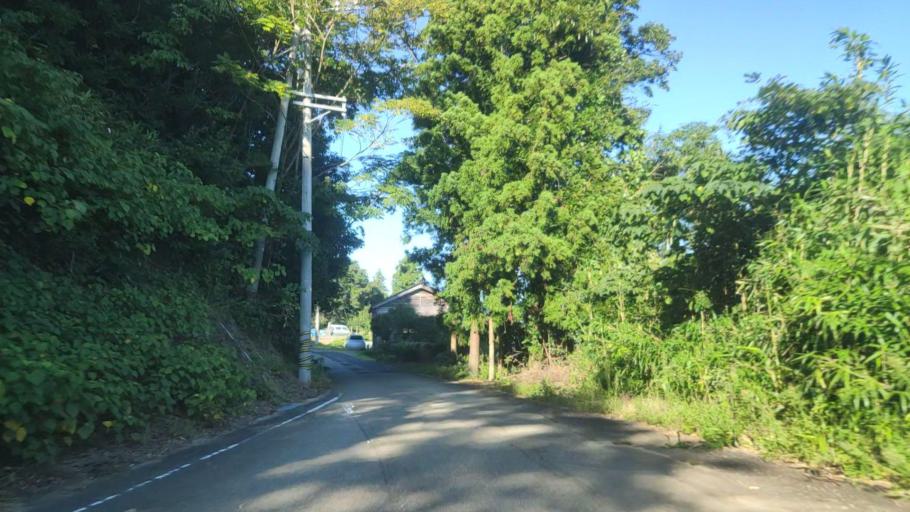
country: JP
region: Ishikawa
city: Nanao
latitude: 37.1189
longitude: 136.8934
